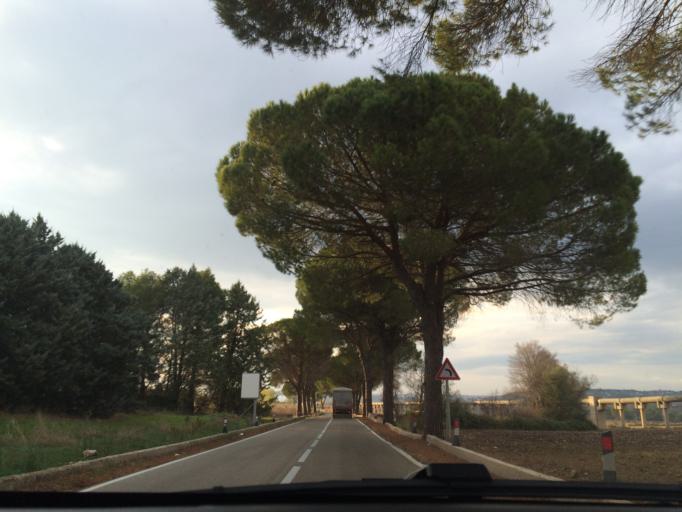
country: IT
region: Basilicate
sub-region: Provincia di Matera
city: Matera
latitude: 40.6788
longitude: 16.6519
